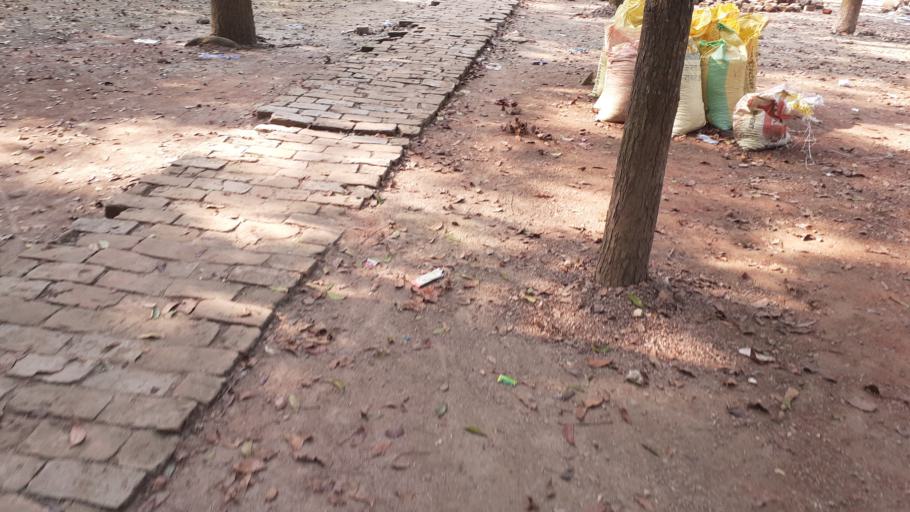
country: IN
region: West Bengal
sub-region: North 24 Parganas
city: Taki
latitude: 22.3791
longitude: 89.1468
